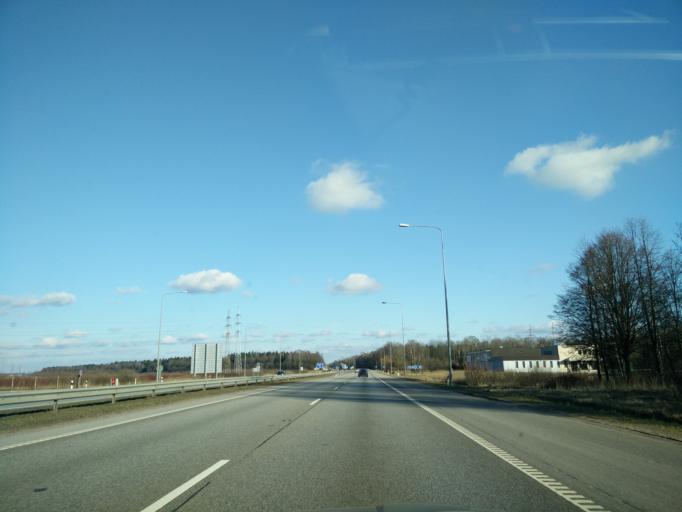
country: LT
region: Kauno apskritis
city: Dainava (Kaunas)
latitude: 54.9315
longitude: 23.9952
